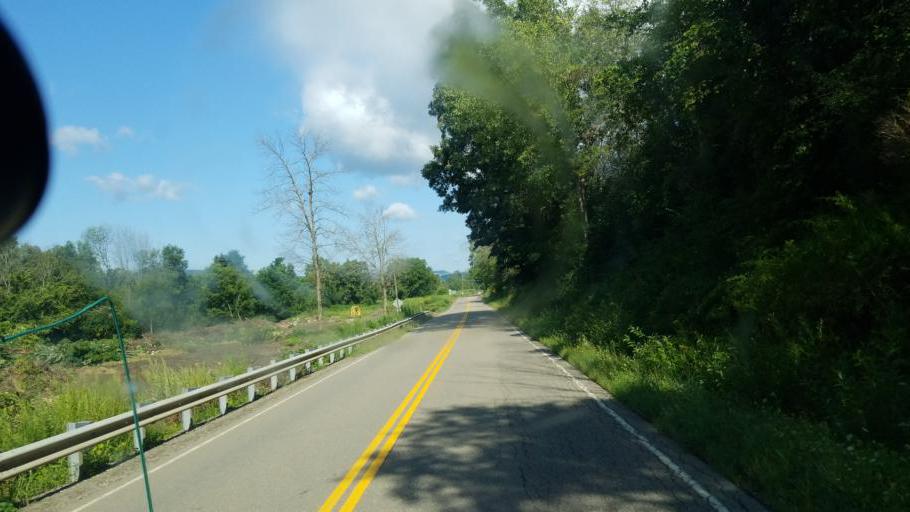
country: US
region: New York
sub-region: Steuben County
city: Canisteo
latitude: 42.2754
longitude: -77.5973
